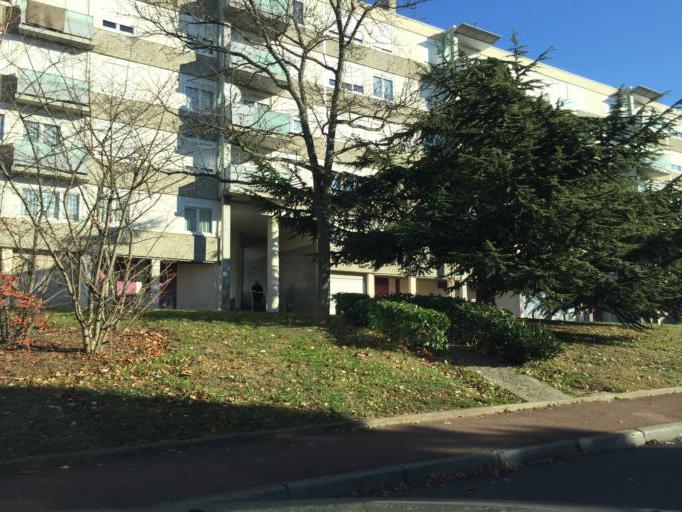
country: FR
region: Rhone-Alpes
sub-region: Departement du Rhone
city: Ecully
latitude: 45.7897
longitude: 4.7916
